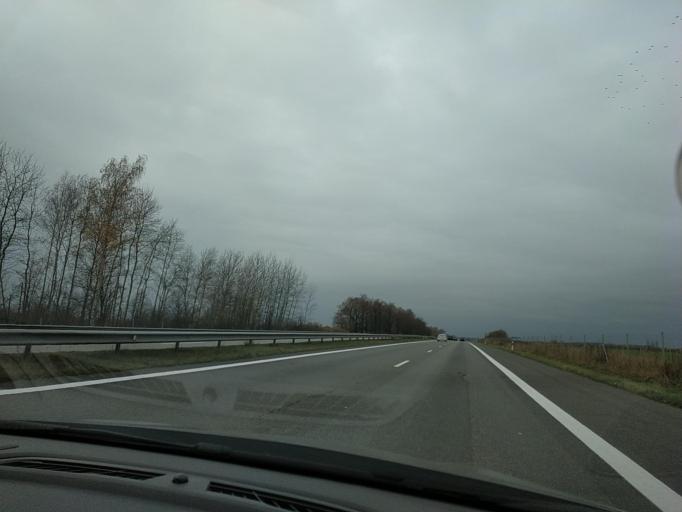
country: LT
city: Kaisiadorys
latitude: 54.8642
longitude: 24.2629
